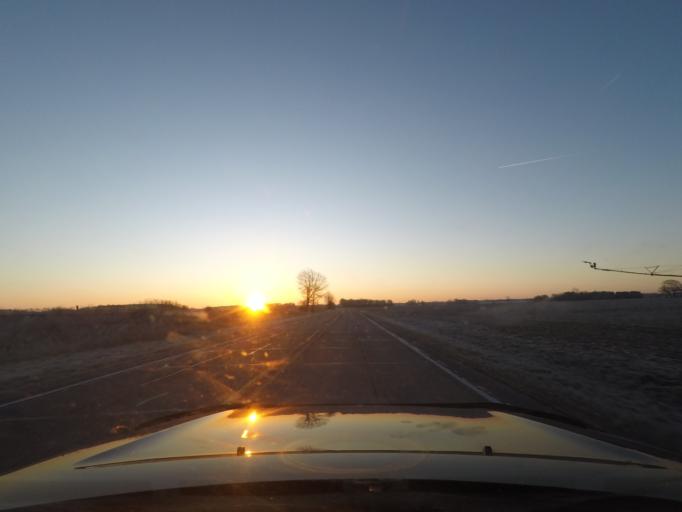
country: US
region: Indiana
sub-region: Saint Joseph County
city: Walkerton
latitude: 41.4737
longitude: -86.5226
